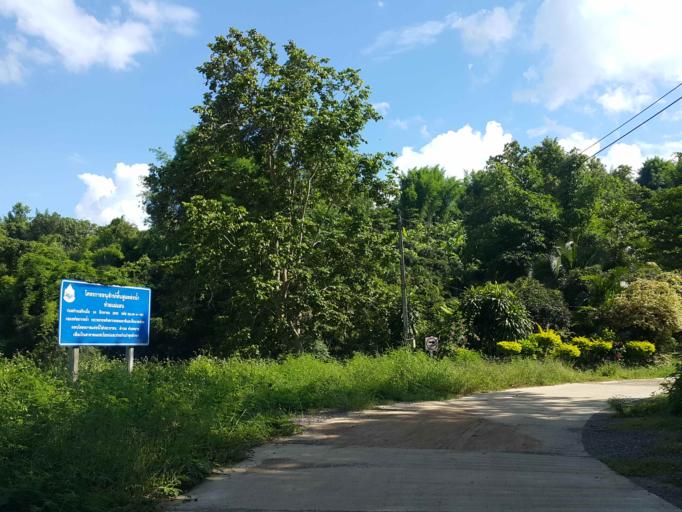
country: TH
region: Chiang Mai
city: Mae Taeng
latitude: 18.9642
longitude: 98.8870
